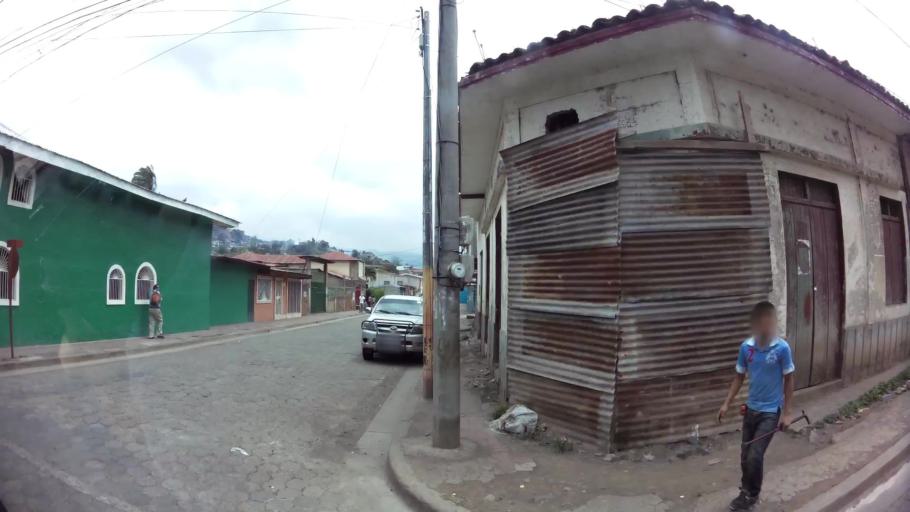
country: NI
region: Matagalpa
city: Matagalpa
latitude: 12.9284
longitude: -85.9140
